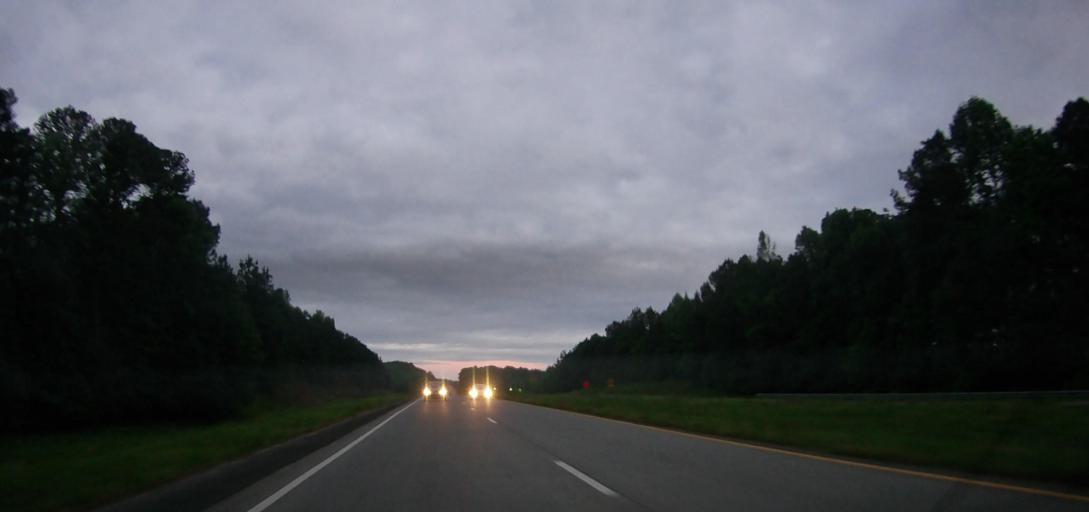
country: US
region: Georgia
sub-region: Jackson County
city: Jefferson
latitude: 34.1279
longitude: -83.6081
